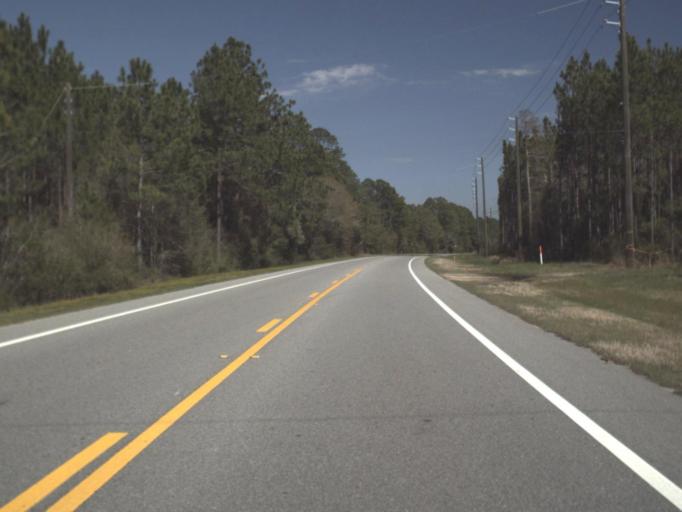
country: US
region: Florida
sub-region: Bay County
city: Lynn Haven
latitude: 30.3283
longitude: -85.7732
